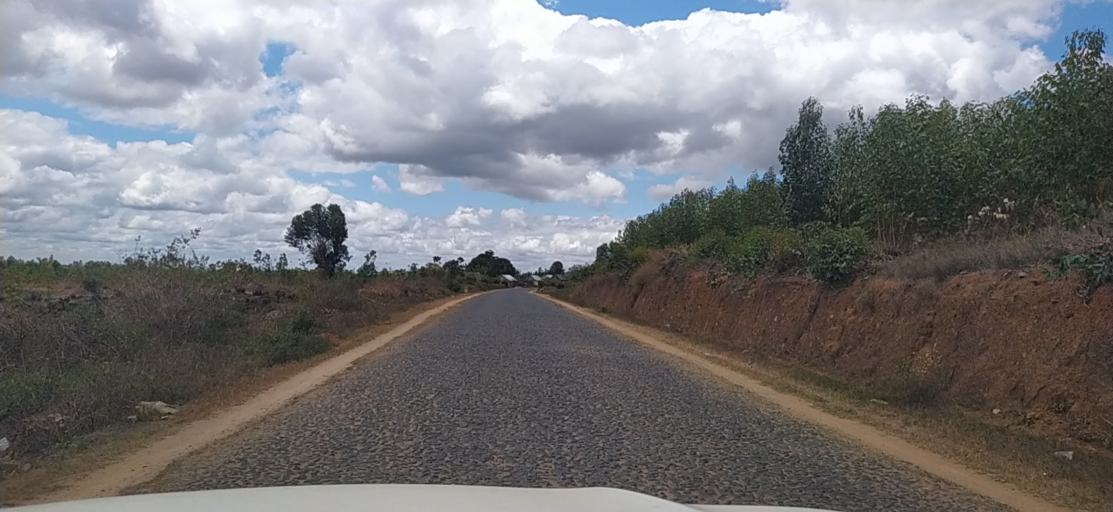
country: MG
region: Alaotra Mangoro
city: Moramanga
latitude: -18.7550
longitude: 48.2594
